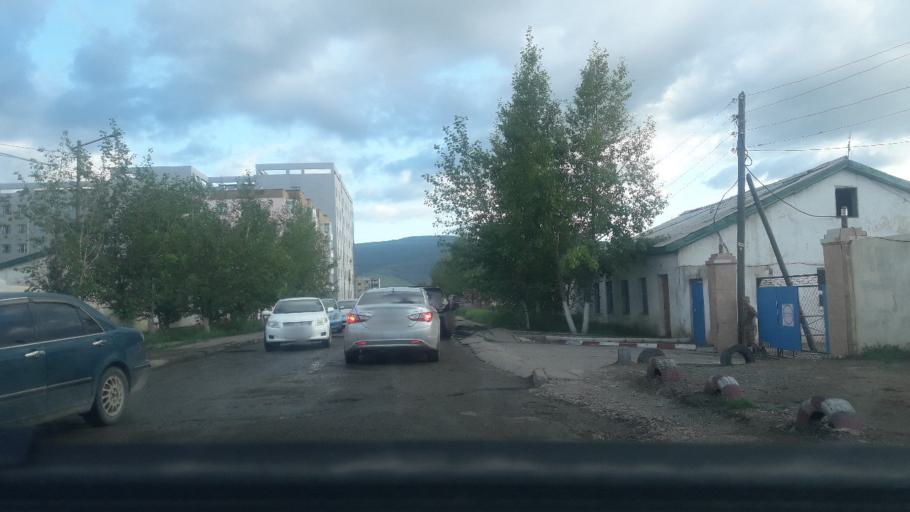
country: MN
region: Ulaanbaatar
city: Ulaanbaatar
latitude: 47.9165
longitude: 106.9945
